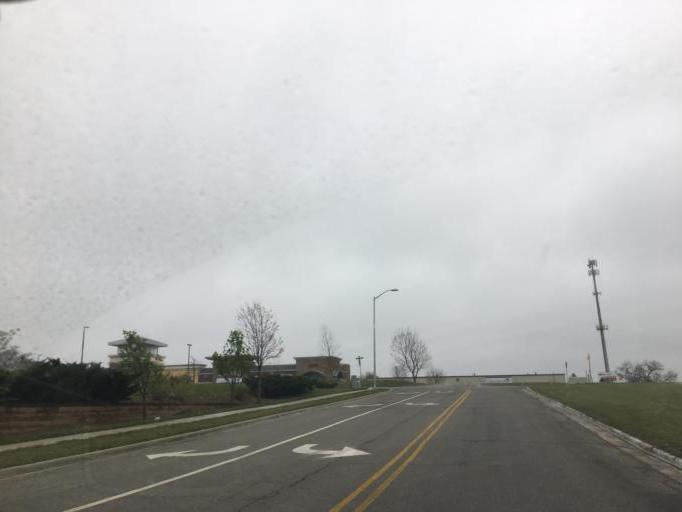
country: US
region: Kansas
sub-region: Johnson County
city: Olathe
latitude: 38.8909
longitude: -94.7971
